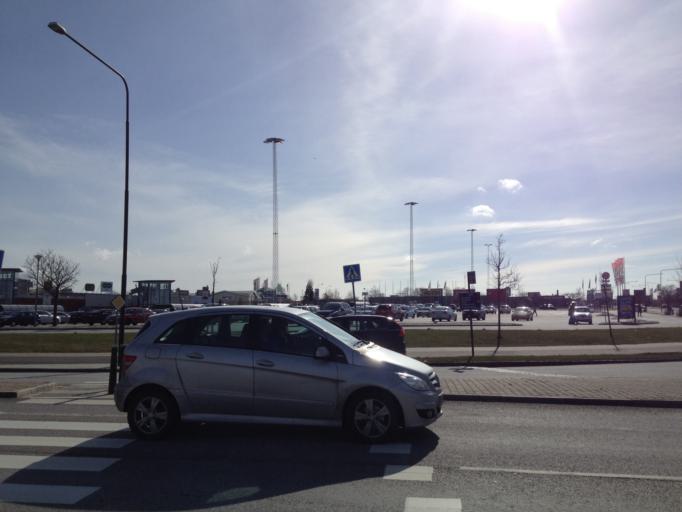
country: SE
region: Skane
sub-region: Malmo
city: Oxie
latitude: 55.5715
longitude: 13.0573
